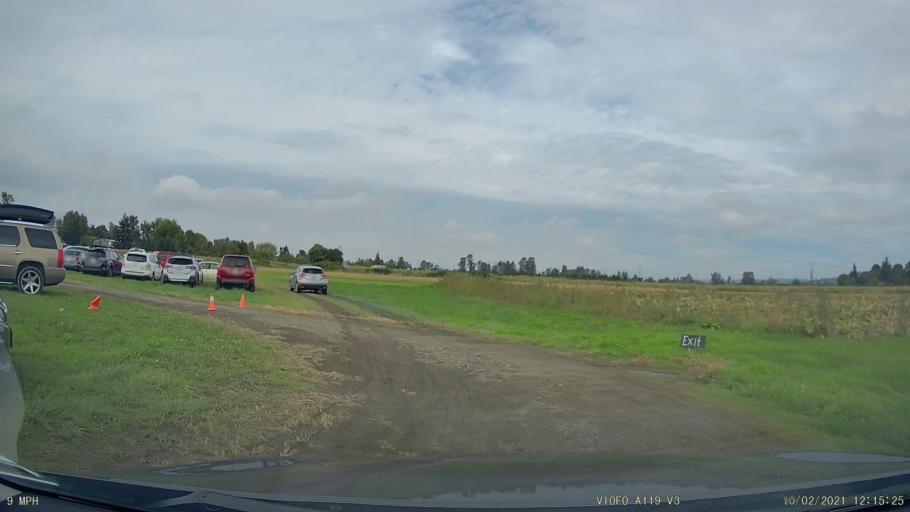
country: US
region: Washington
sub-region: Snohomish County
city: Fobes Hill
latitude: 47.9330
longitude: -122.1646
